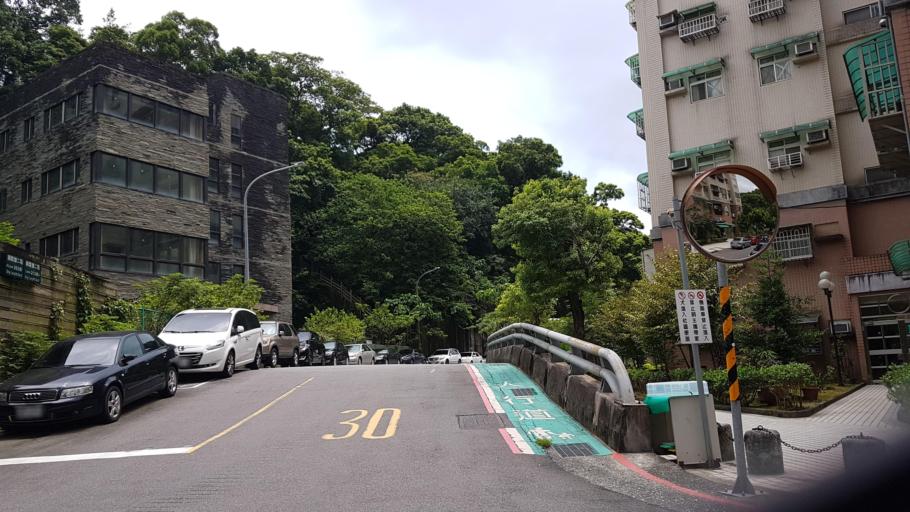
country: TW
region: Taipei
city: Taipei
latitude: 25.0027
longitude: 121.5483
